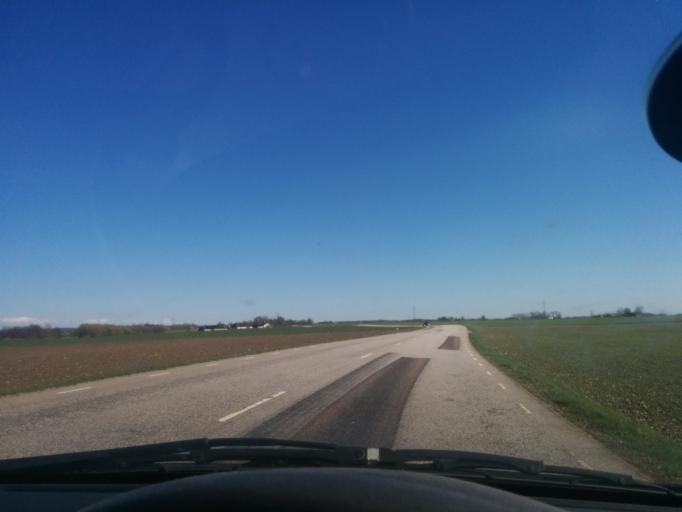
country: SE
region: Skane
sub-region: Svedala Kommun
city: Klagerup
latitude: 55.6308
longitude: 13.2929
